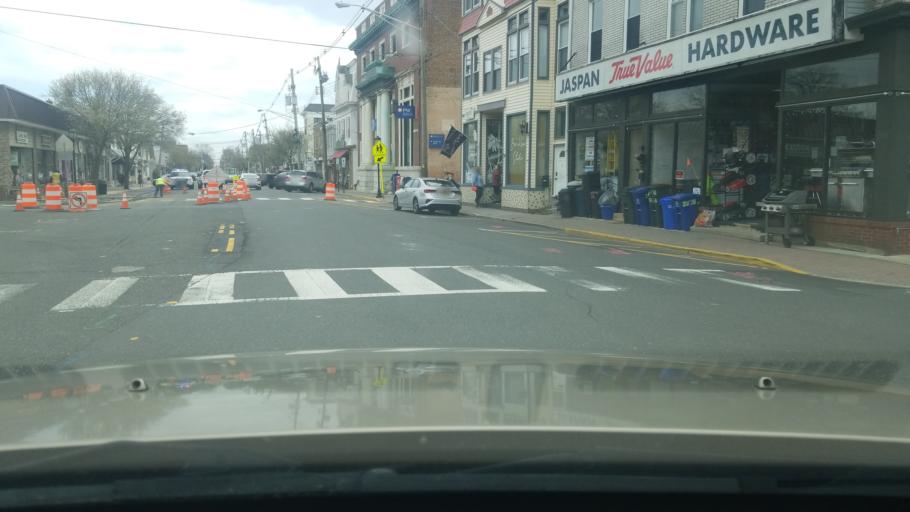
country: US
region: New Jersey
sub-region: Monmouth County
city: Manasquan
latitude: 40.1239
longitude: -74.0516
